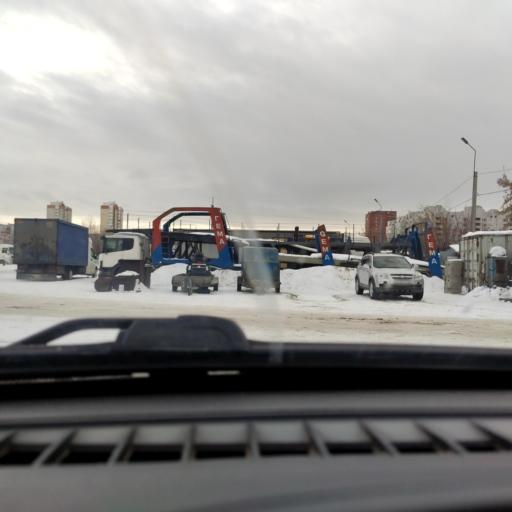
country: RU
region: Samara
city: Tol'yatti
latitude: 53.5518
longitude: 49.3285
